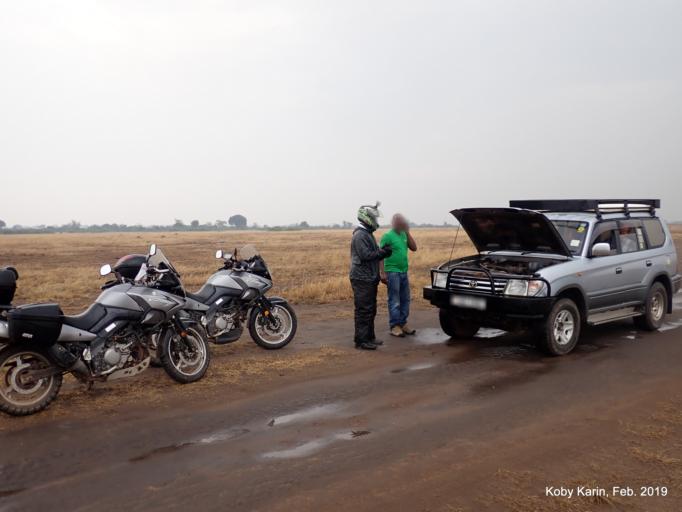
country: UG
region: Western Region
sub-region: Kasese District
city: Kasese
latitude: -0.0292
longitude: 30.0491
